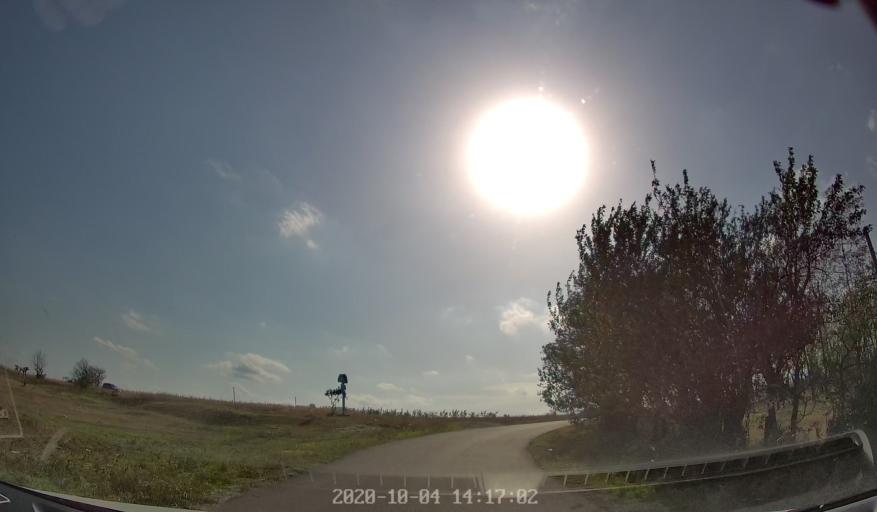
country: MD
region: Rezina
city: Saharna
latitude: 47.6020
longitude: 28.9841
